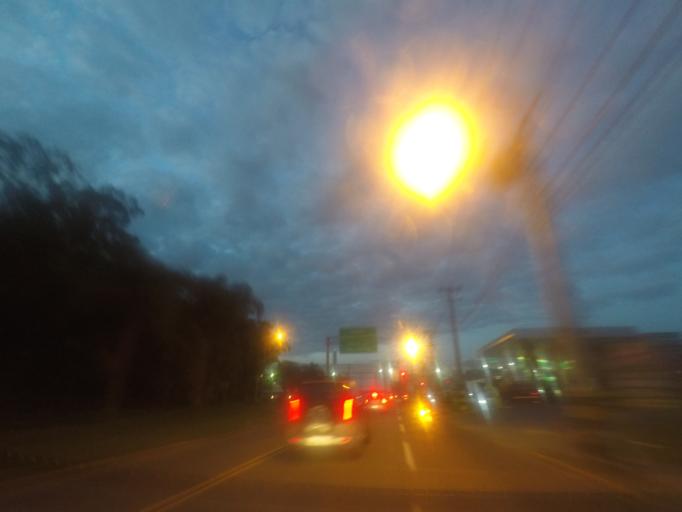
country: BR
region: Parana
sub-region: Pinhais
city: Pinhais
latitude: -25.3922
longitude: -49.1878
